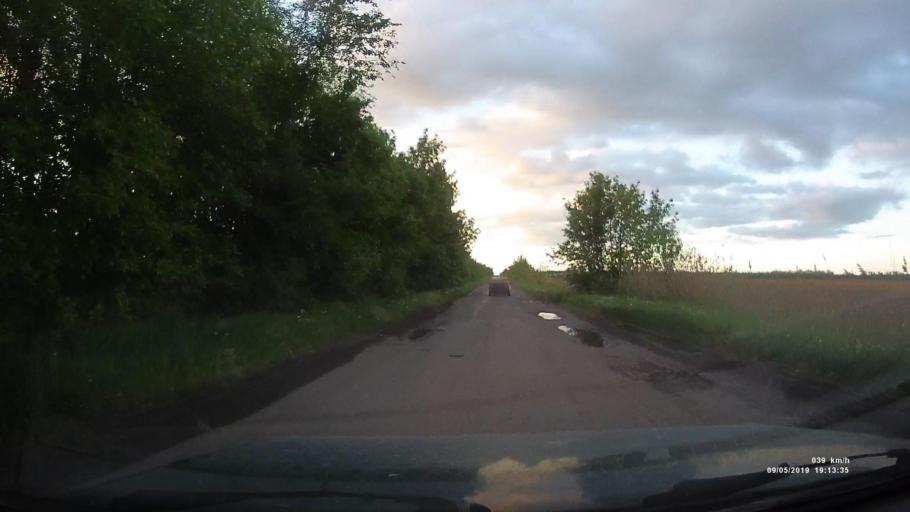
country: RU
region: Krasnodarskiy
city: Kanelovskaya
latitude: 46.7517
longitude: 39.2138
